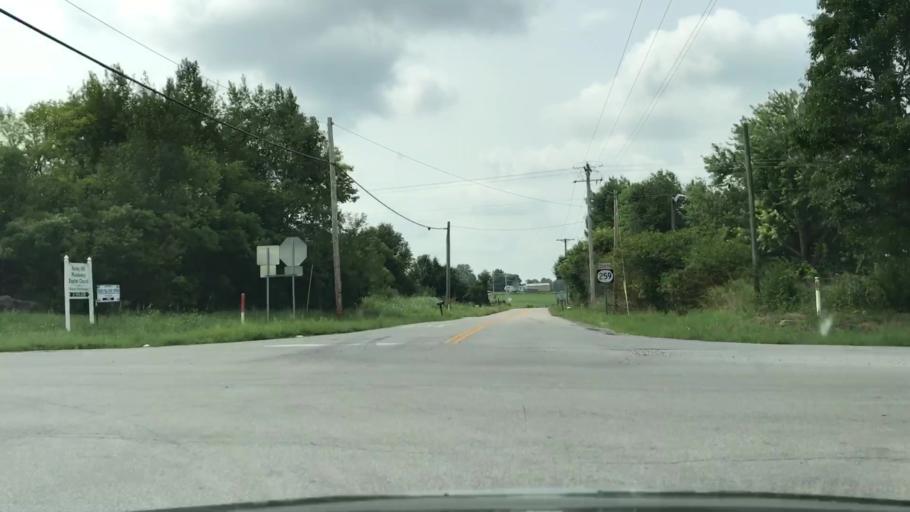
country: US
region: Kentucky
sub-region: Edmonson County
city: Brownsville
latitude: 37.0923
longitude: -86.1475
